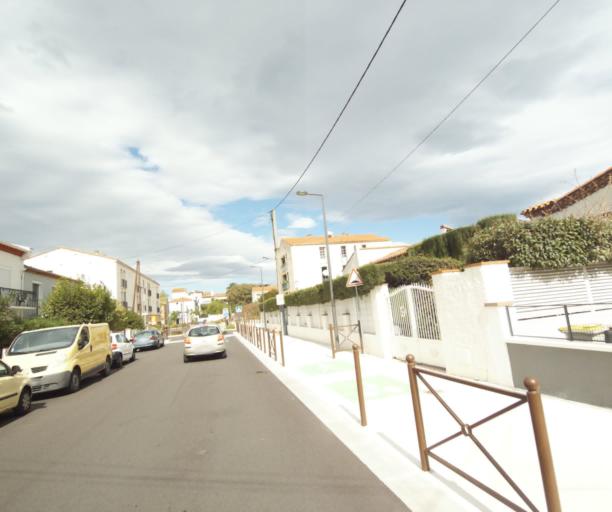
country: FR
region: Languedoc-Roussillon
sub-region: Departement des Pyrenees-Orientales
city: Argelers
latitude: 42.5449
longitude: 3.0254
